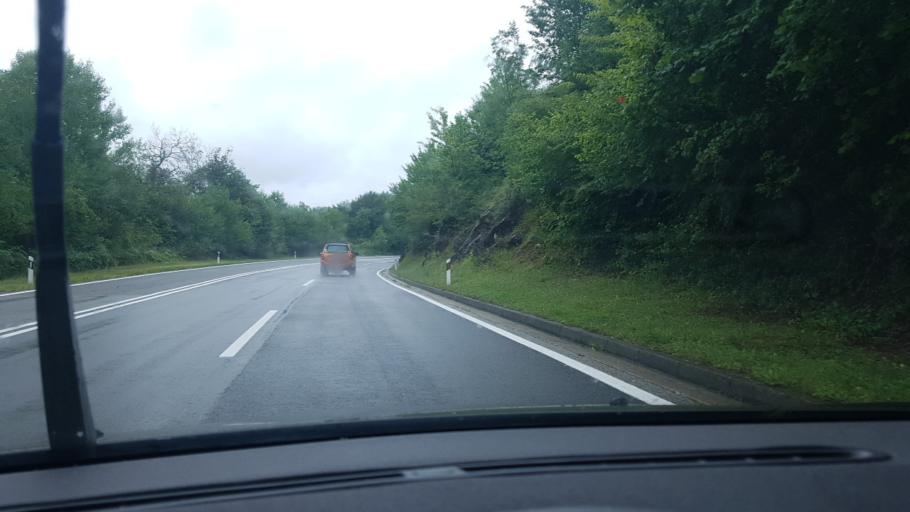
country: HR
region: Karlovacka
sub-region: Grad Karlovac
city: Slunj
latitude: 45.0729
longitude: 15.5815
